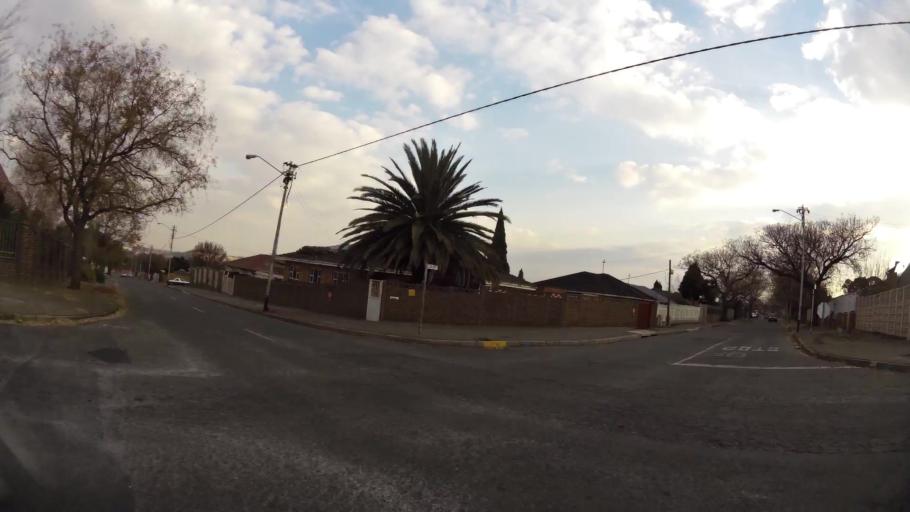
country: ZA
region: Gauteng
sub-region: Ekurhuleni Metropolitan Municipality
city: Germiston
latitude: -26.1774
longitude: 28.1728
